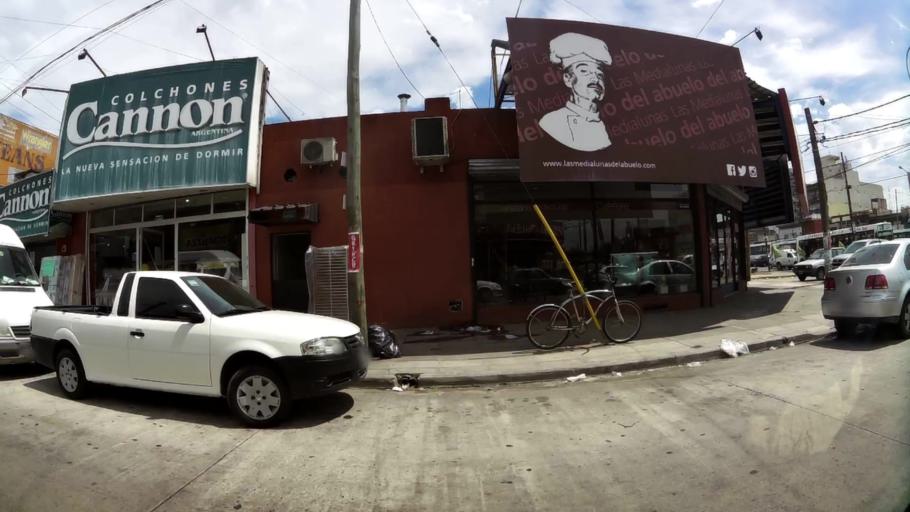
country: AR
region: Buenos Aires
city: San Justo
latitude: -34.6830
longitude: -58.5547
